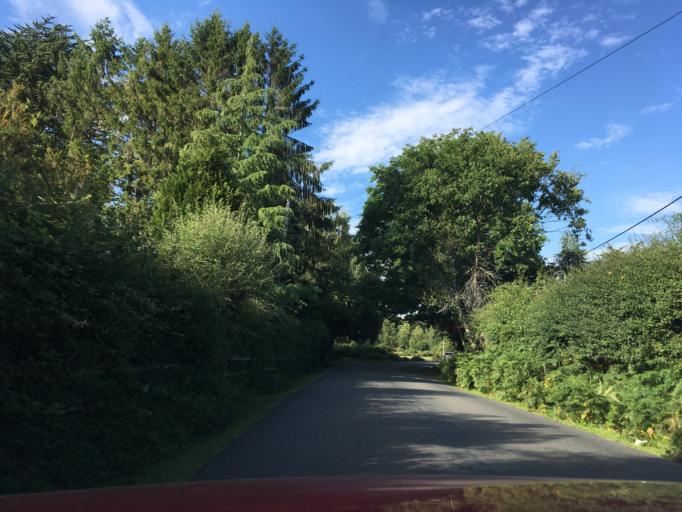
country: GB
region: England
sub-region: Hampshire
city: West Wellow
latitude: 50.9485
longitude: -1.5921
